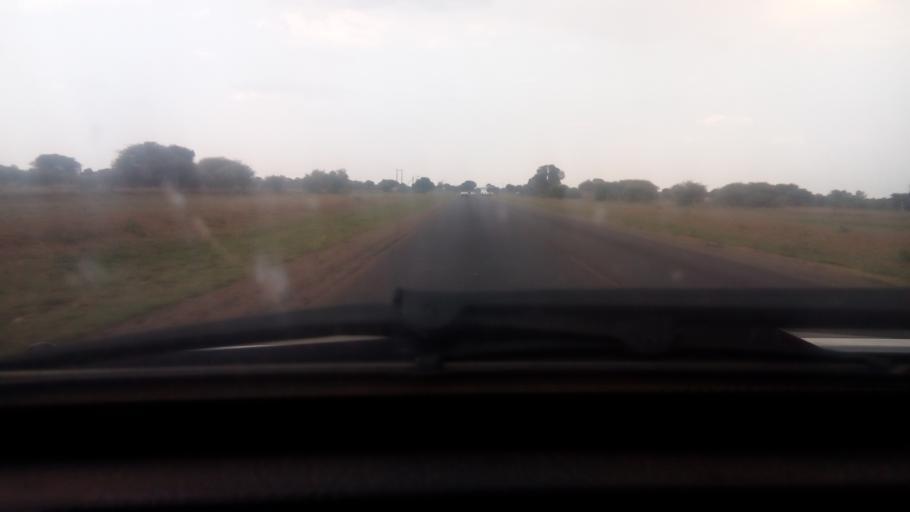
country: BW
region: Kweneng
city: Metsemotlhaba
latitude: -24.4769
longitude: 25.7217
